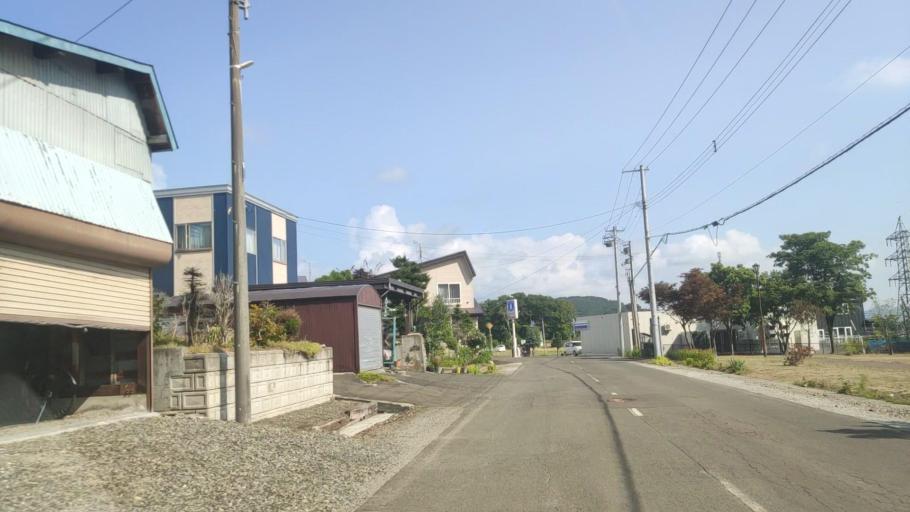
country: JP
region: Hokkaido
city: Shimo-furano
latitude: 43.3432
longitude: 142.3704
